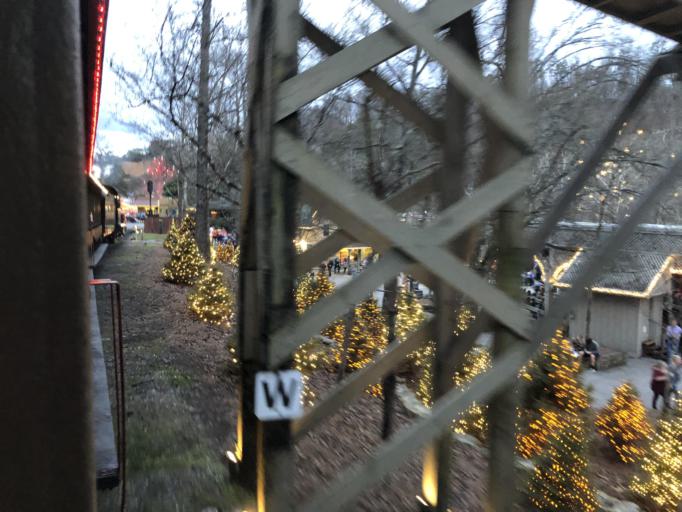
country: US
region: Tennessee
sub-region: Sevier County
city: Pigeon Forge
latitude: 35.7933
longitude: -83.5337
